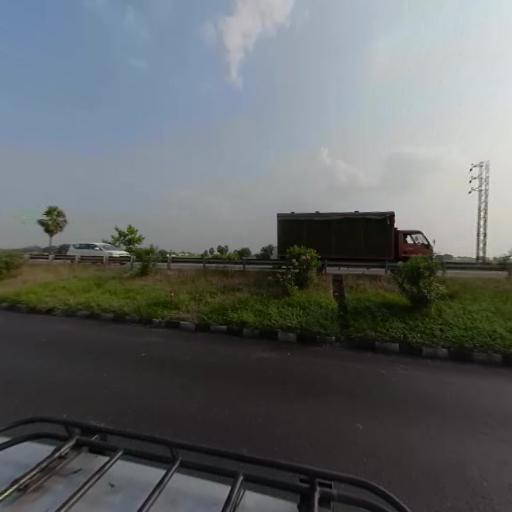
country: IN
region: Telangana
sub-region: Nalgonda
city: Suriapet
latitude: 17.1718
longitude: 79.5034
